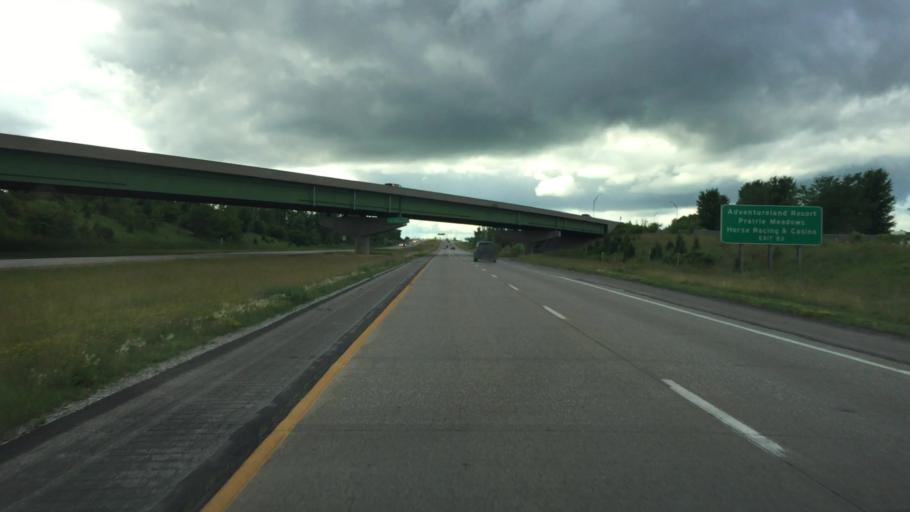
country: US
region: Iowa
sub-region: Polk County
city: Altoona
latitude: 41.6322
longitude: -93.5025
